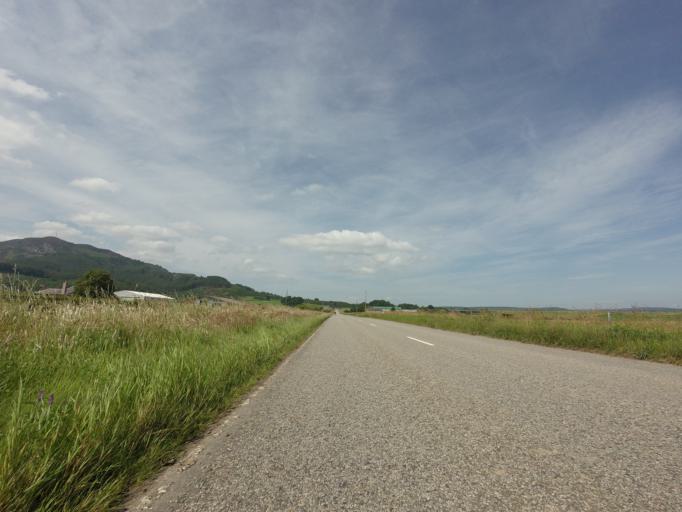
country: GB
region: Scotland
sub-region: Highland
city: Tain
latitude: 57.8443
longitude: -4.1977
